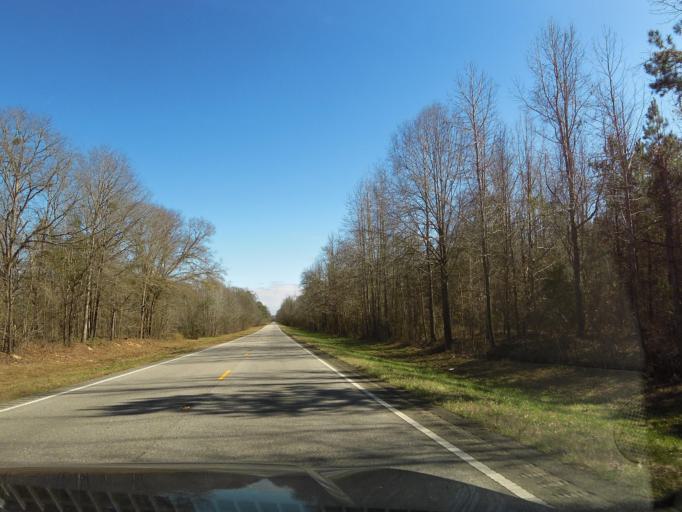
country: US
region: Alabama
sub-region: Barbour County
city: Clayton
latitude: 32.0524
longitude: -85.4437
